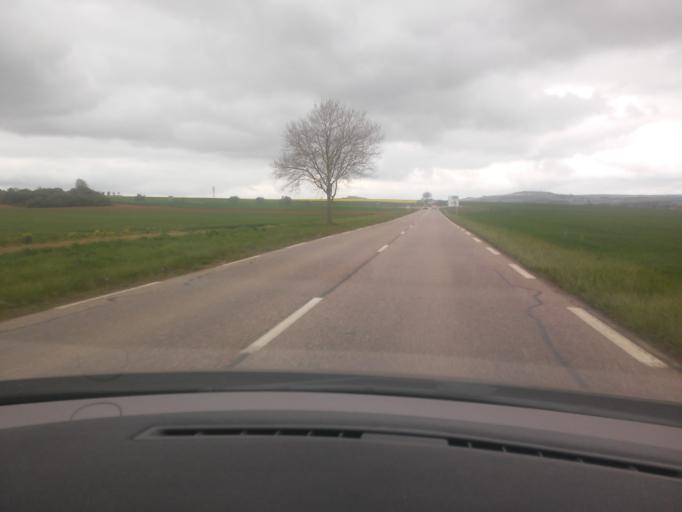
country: FR
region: Lorraine
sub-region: Departement de la Moselle
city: Verny
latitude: 48.9537
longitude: 6.1718
